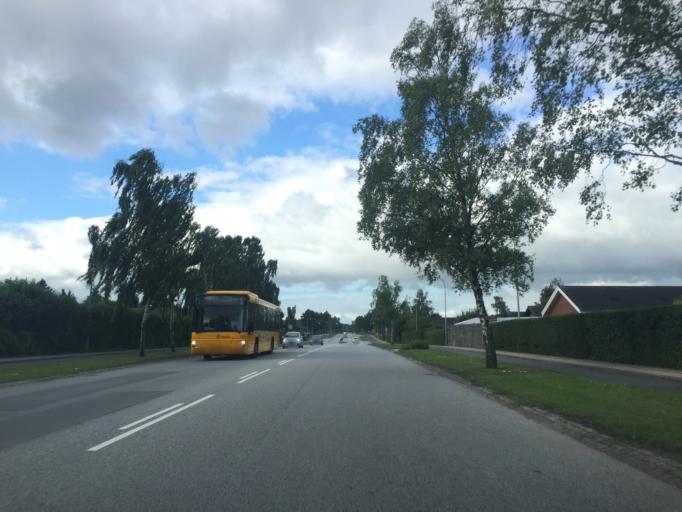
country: DK
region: Capital Region
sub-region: Brondby Kommune
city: Brondbyvester
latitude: 55.6600
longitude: 12.4326
